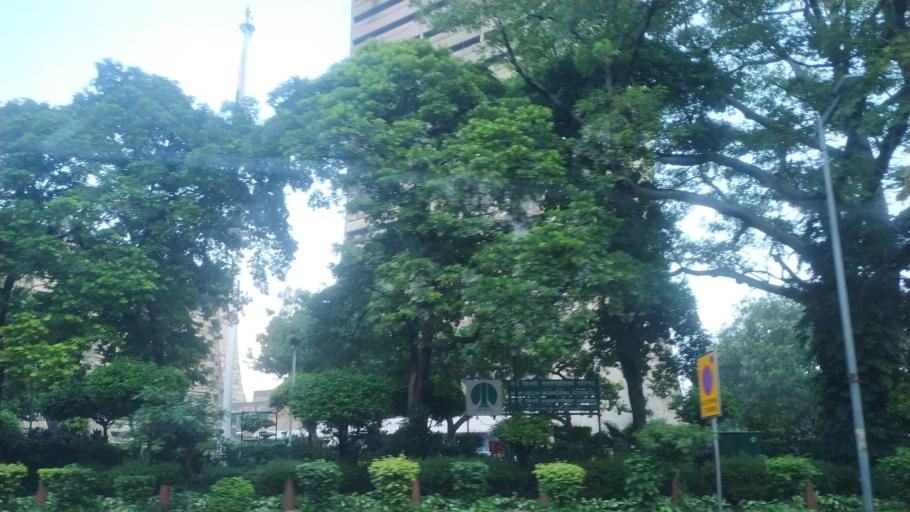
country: IN
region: NCT
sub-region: New Delhi
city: New Delhi
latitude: 28.6281
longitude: 77.2161
